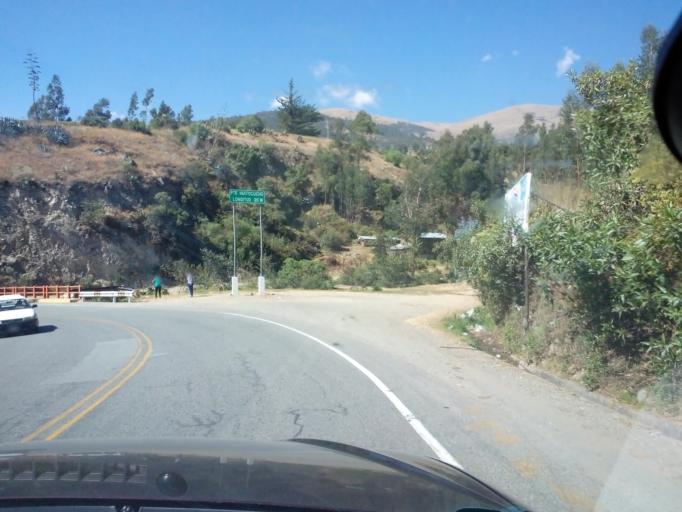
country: PE
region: Apurimac
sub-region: Provincia de Abancay
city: Curahuasi
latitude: -13.5624
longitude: -72.7556
